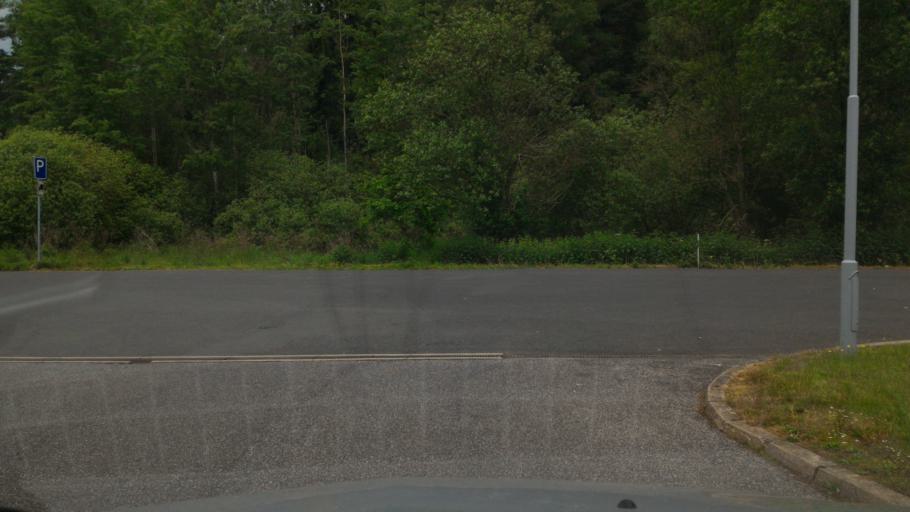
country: CZ
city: Jablonne v Podjestedi
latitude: 50.7877
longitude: 14.8091
